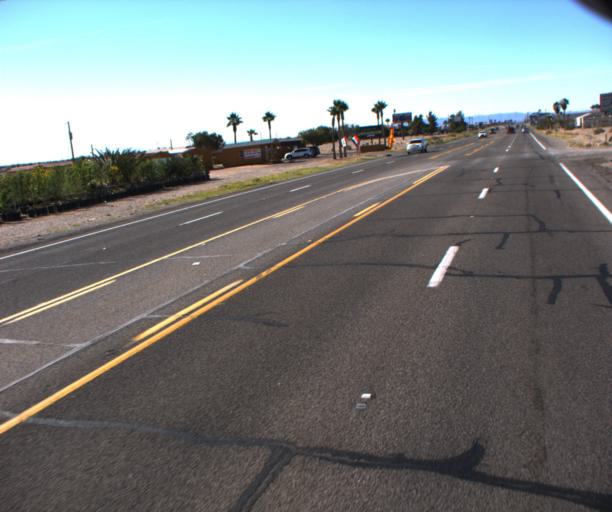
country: US
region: Arizona
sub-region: Mohave County
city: Mohave Valley
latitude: 35.0081
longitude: -114.5981
